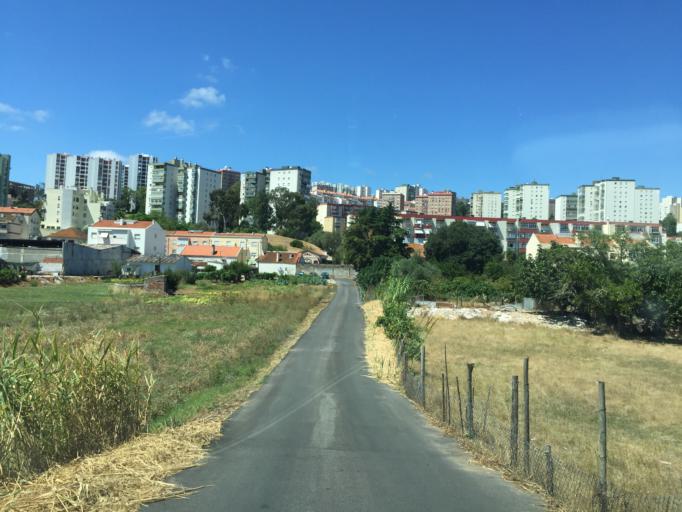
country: PT
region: Lisbon
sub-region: Odivelas
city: Povoa de Santo Adriao
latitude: 38.8092
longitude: -9.1552
